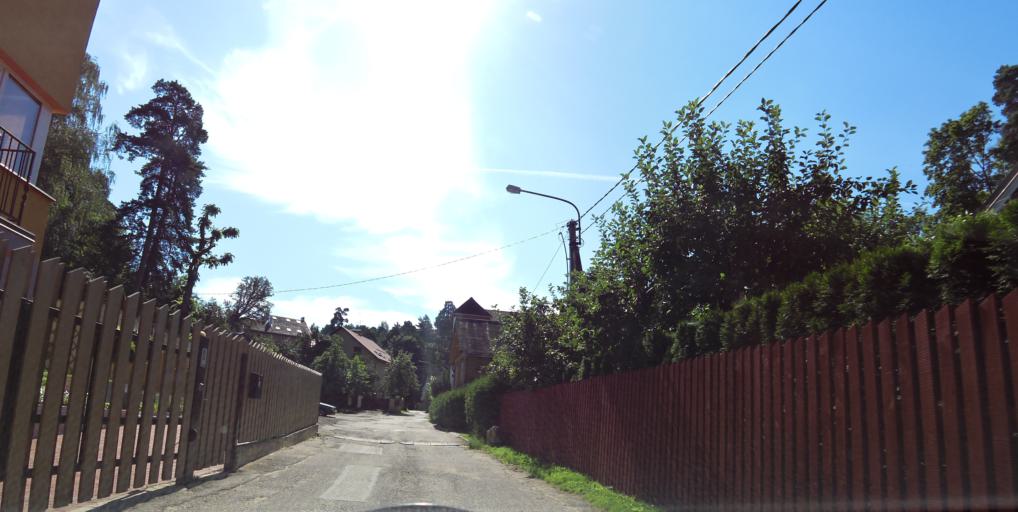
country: LT
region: Vilnius County
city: Rasos
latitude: 54.6930
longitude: 25.3117
